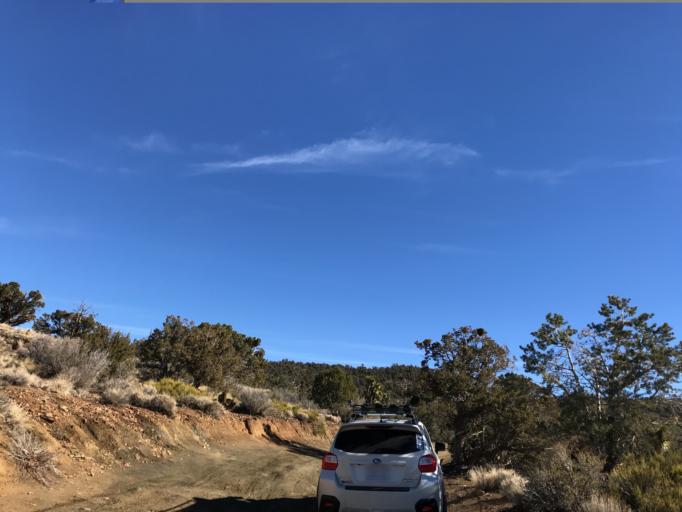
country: US
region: California
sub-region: San Bernardino County
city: Big Bear City
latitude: 34.2514
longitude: -116.7258
